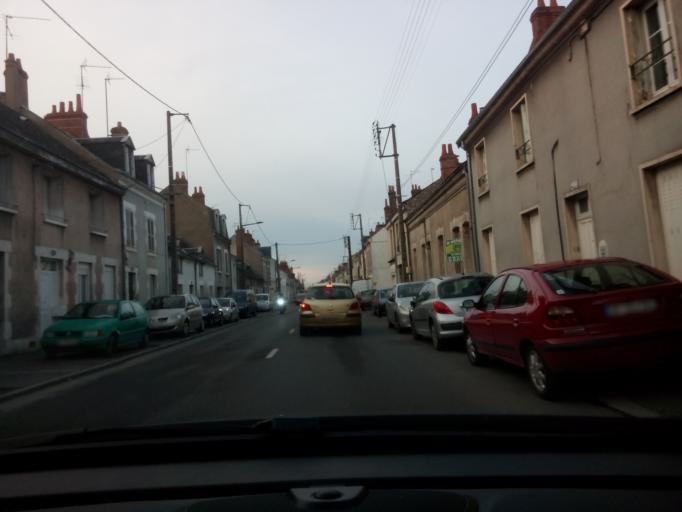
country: FR
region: Centre
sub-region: Departement du Loiret
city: Orleans
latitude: 47.9202
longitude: 1.8981
